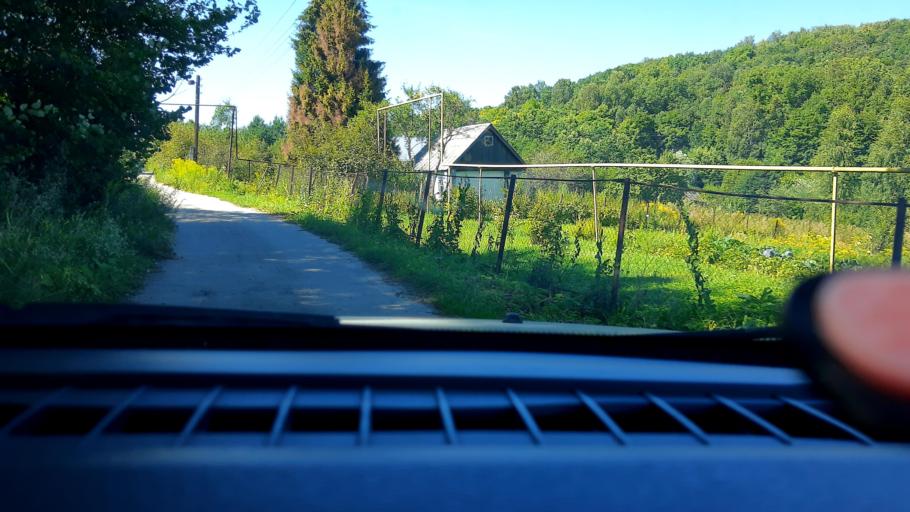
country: RU
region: Nizjnij Novgorod
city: Afonino
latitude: 56.2390
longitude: 44.0351
